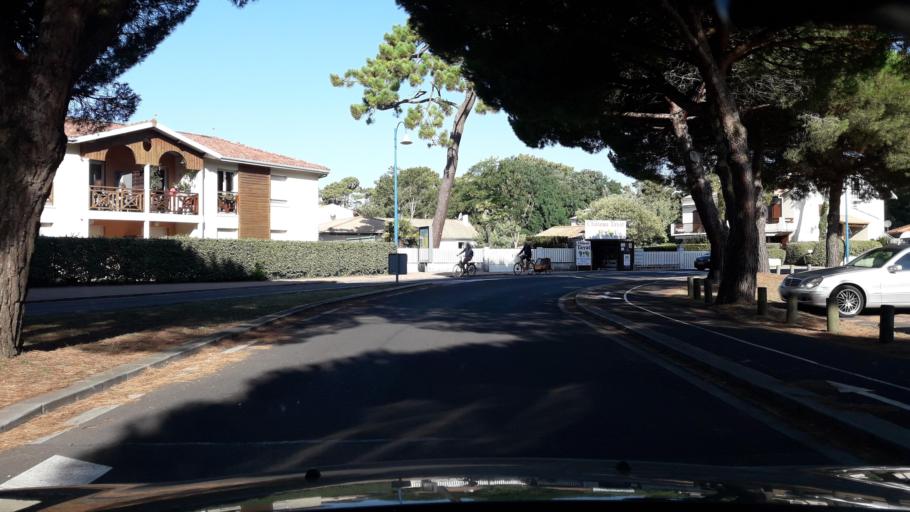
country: FR
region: Poitou-Charentes
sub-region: Departement de la Charente-Maritime
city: Les Mathes
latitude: 45.6915
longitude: -1.1790
